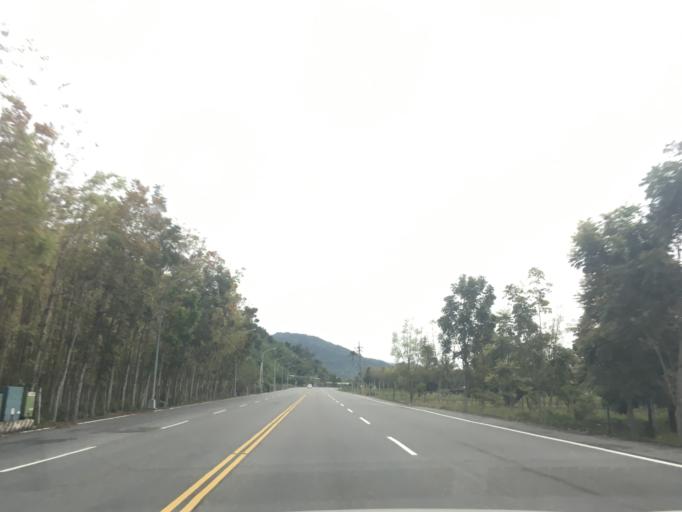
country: TW
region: Taiwan
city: Taitung City
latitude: 22.7365
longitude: 121.0566
